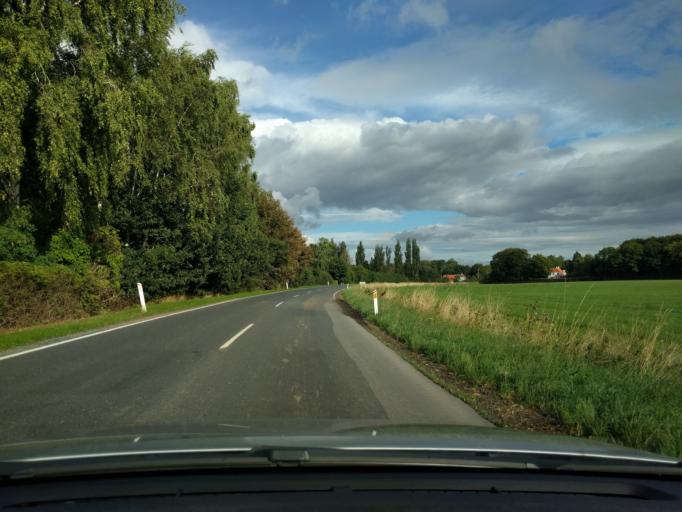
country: DK
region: South Denmark
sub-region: Kerteminde Kommune
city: Kerteminde
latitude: 55.4066
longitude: 10.6623
